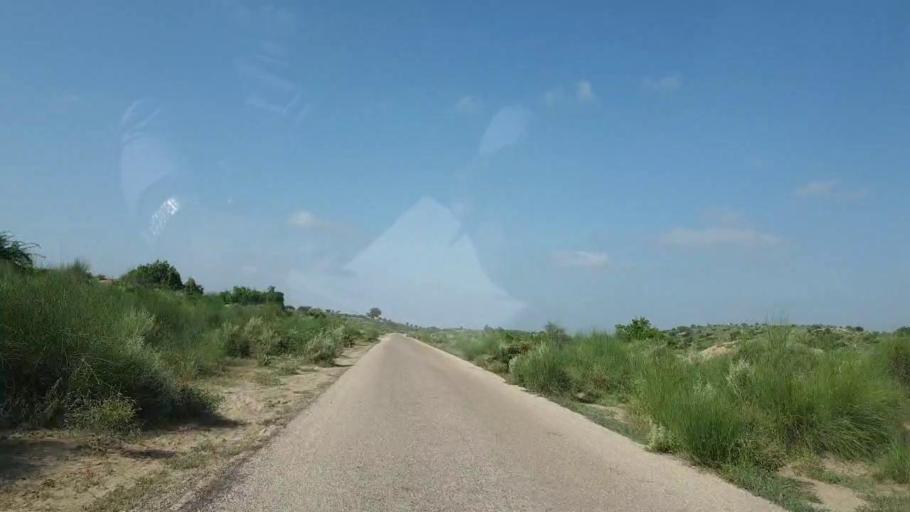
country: PK
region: Sindh
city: Mithi
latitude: 24.5629
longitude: 69.9088
